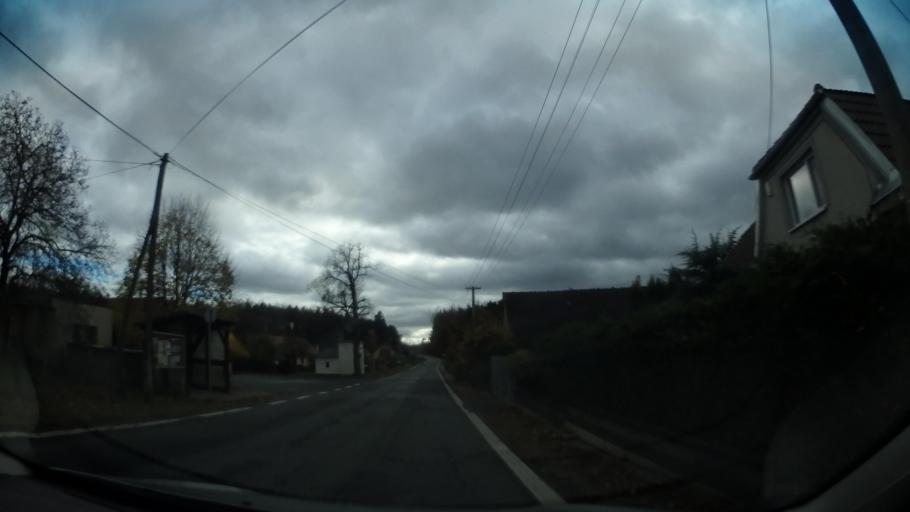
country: CZ
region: Vysocina
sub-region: Okres Zd'ar nad Sazavou
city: Velka Bites
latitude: 49.2549
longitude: 16.2576
